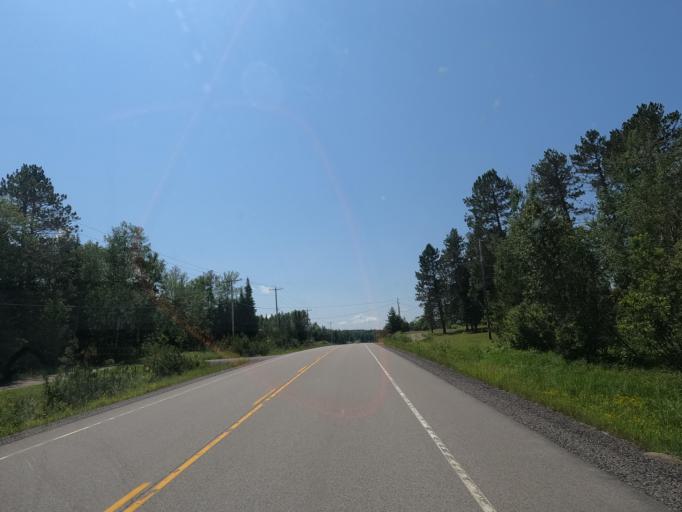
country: CA
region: Ontario
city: Dryden
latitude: 49.8742
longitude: -93.3591
